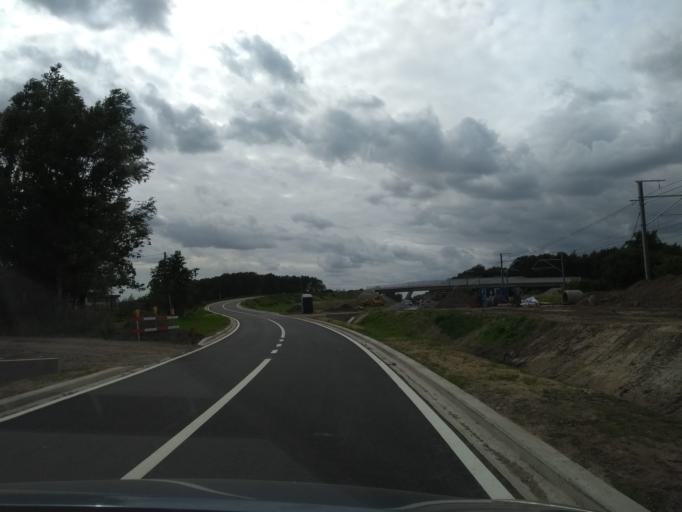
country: BE
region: Flanders
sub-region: Provincie Oost-Vlaanderen
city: Nevele
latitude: 51.0787
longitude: 3.5094
